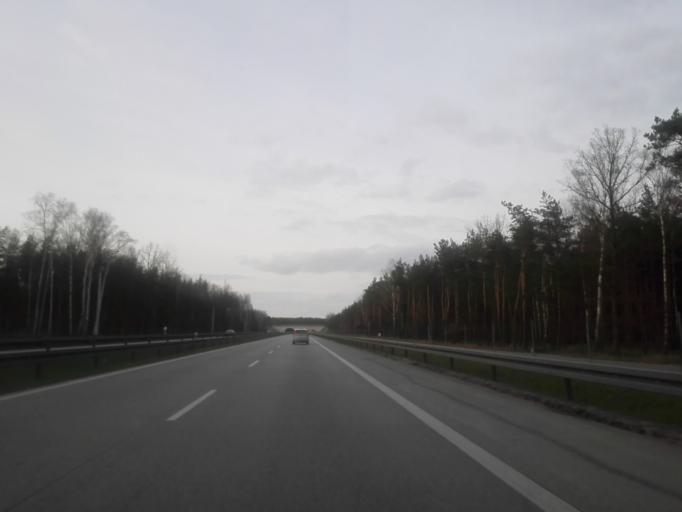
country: PL
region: Lodz Voivodeship
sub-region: Powiat tomaszowski
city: Tomaszow Mazowiecki
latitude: 51.5721
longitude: 20.0265
